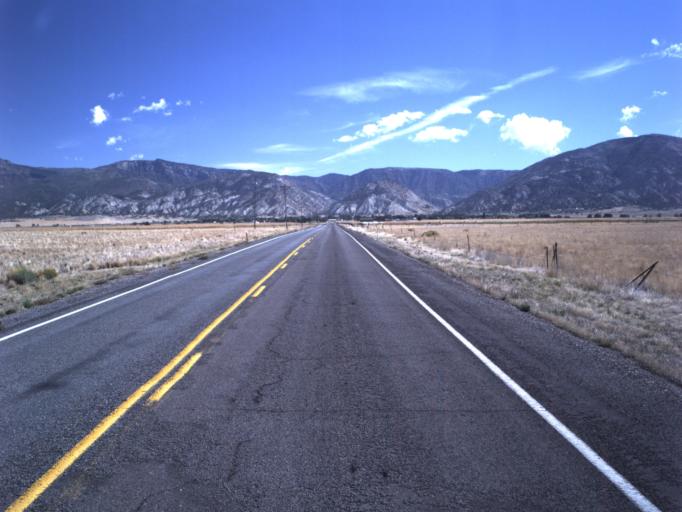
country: US
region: Utah
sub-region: Juab County
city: Nephi
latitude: 39.5578
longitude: -111.9134
